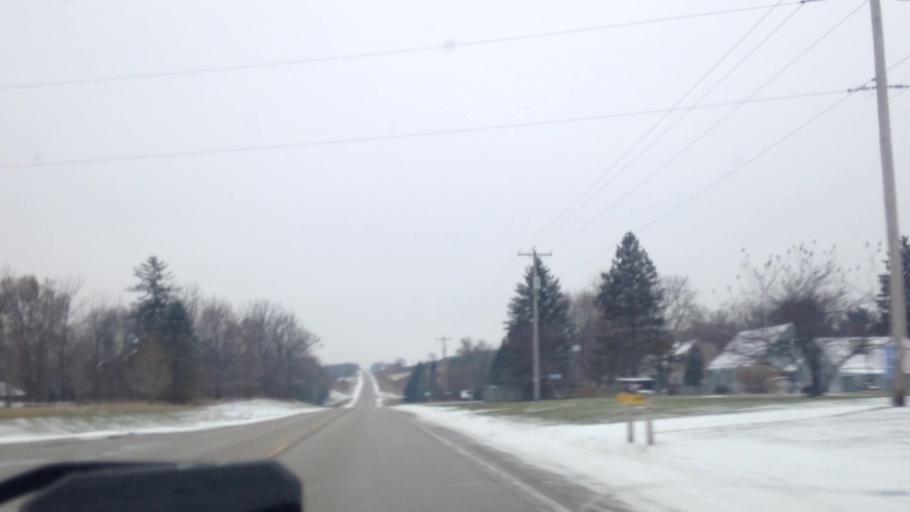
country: US
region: Wisconsin
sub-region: Dodge County
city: Hustisford
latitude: 43.2831
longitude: -88.5185
